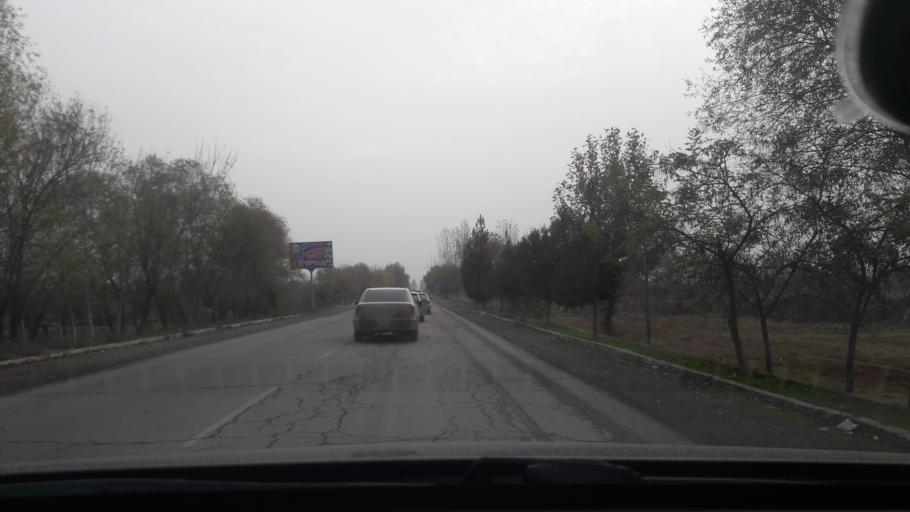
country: TJ
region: Khatlon
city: Qurghonteppa
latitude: 37.8656
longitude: 68.7163
